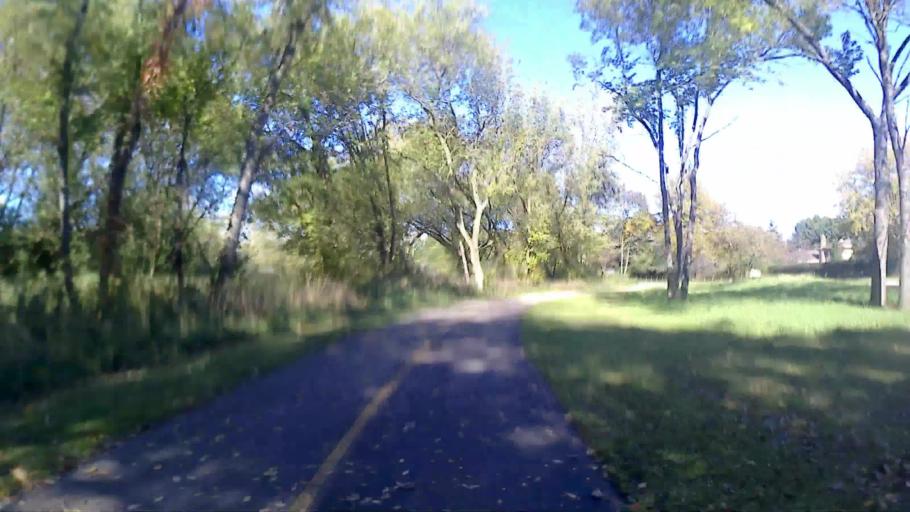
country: US
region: Illinois
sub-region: DuPage County
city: Itasca
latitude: 42.0097
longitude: -88.0192
